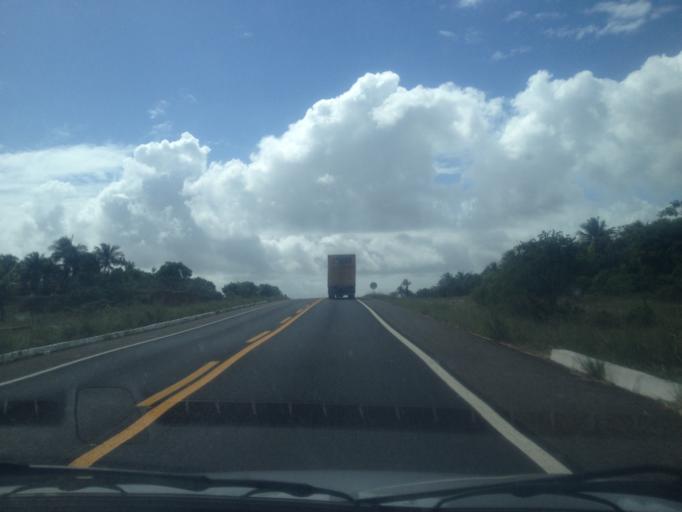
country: BR
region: Sergipe
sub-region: Indiaroba
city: Indiaroba
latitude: -11.6368
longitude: -37.5398
